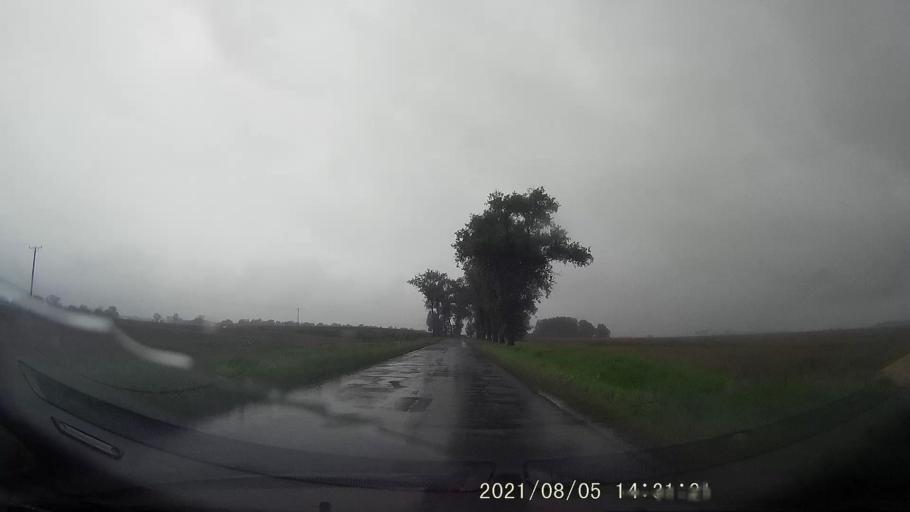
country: PL
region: Opole Voivodeship
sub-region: Powiat nyski
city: Korfantow
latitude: 50.4760
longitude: 17.5577
